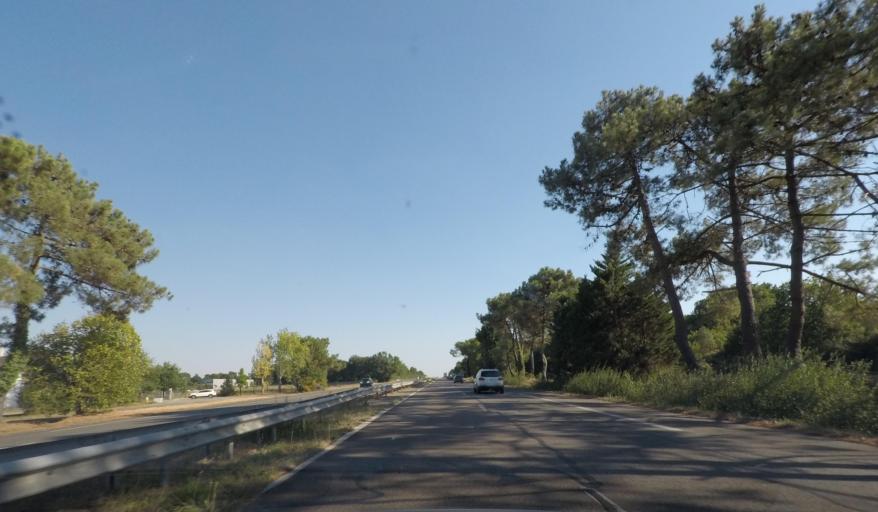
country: FR
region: Pays de la Loire
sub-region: Departement de la Loire-Atlantique
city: Saint-Brevin-les-Pins
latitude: 47.2345
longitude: -2.1572
